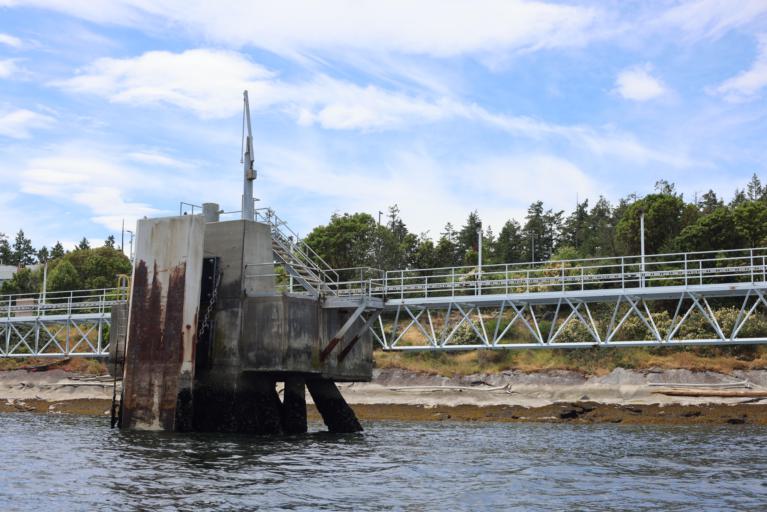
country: CA
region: British Columbia
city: Nanaimo
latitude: 49.1643
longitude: -123.8913
